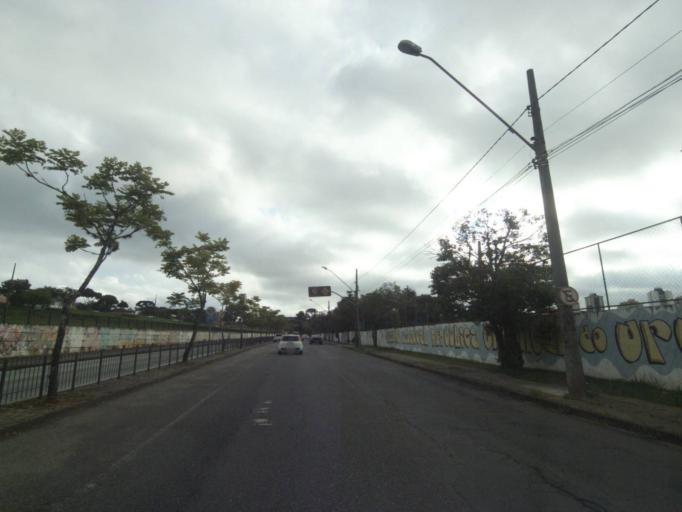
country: BR
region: Parana
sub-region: Pinhais
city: Pinhais
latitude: -25.4402
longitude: -49.2283
